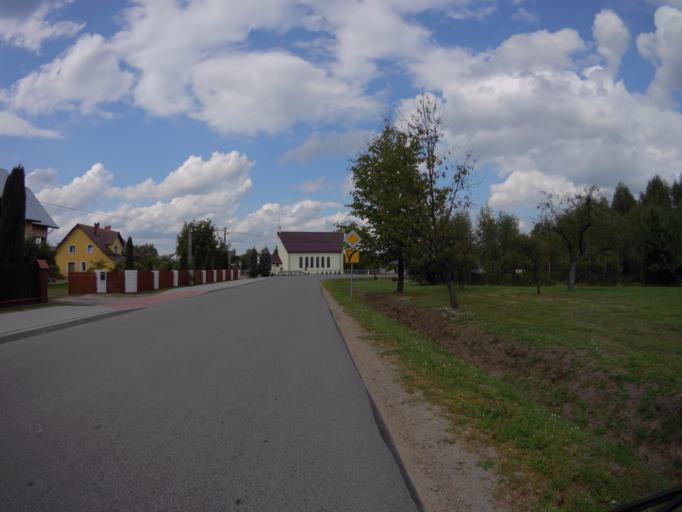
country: PL
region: Subcarpathian Voivodeship
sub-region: Powiat lezajski
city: Brzoza Krolewska
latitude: 50.2667
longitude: 22.3468
